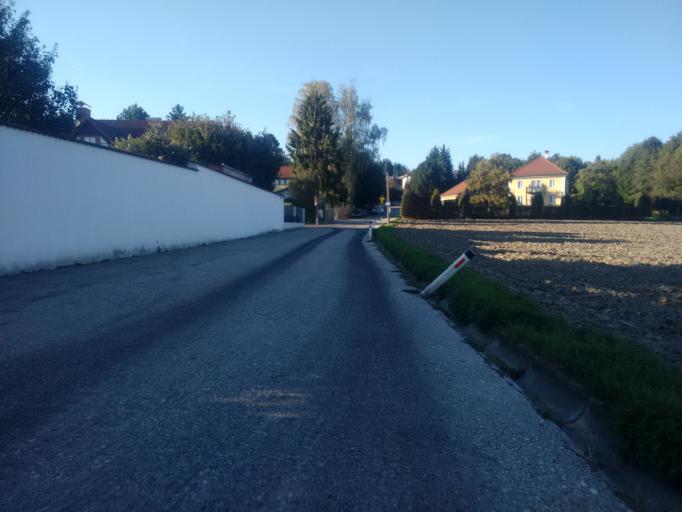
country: AT
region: Upper Austria
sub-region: Wels Stadt
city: Wels
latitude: 48.1826
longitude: 13.9922
